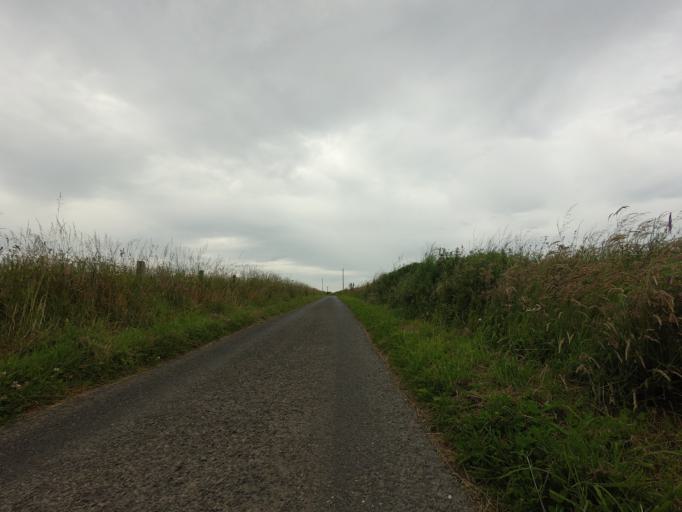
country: GB
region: Scotland
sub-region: Aberdeenshire
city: Whitehills
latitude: 57.6753
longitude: -2.5972
